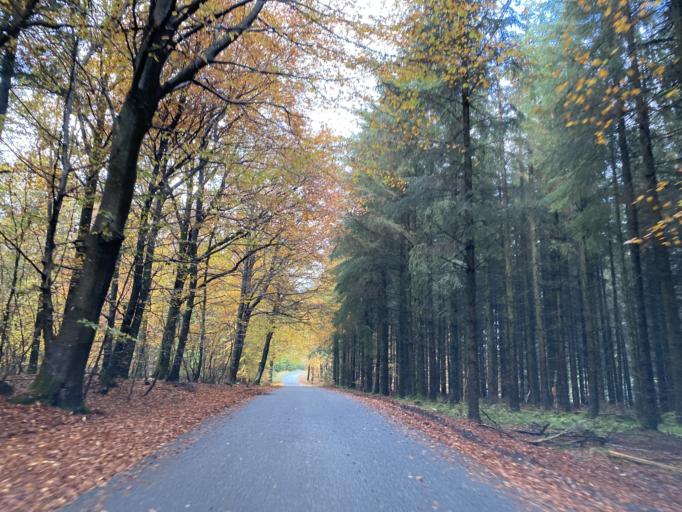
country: DK
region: Central Jutland
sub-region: Skanderborg Kommune
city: Galten
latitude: 56.2291
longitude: 9.9295
